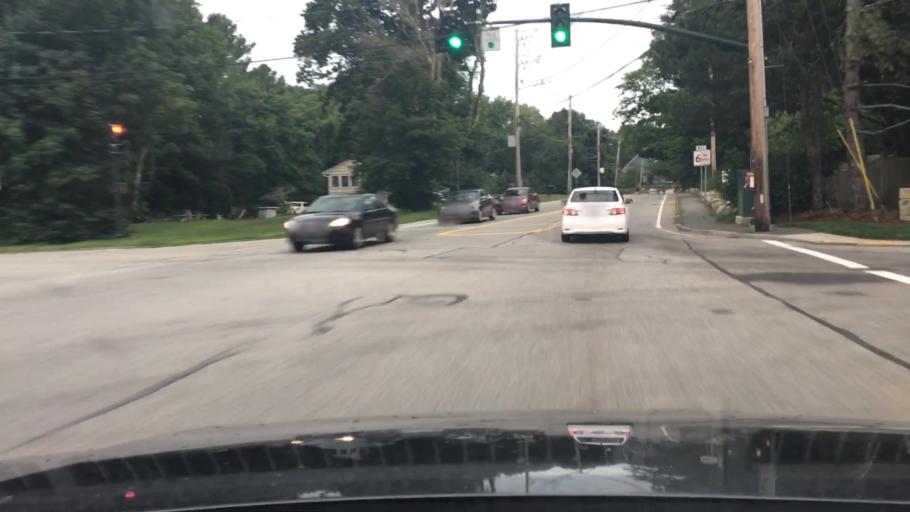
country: US
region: Massachusetts
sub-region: Middlesex County
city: North Reading
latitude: 42.5725
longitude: -71.1004
